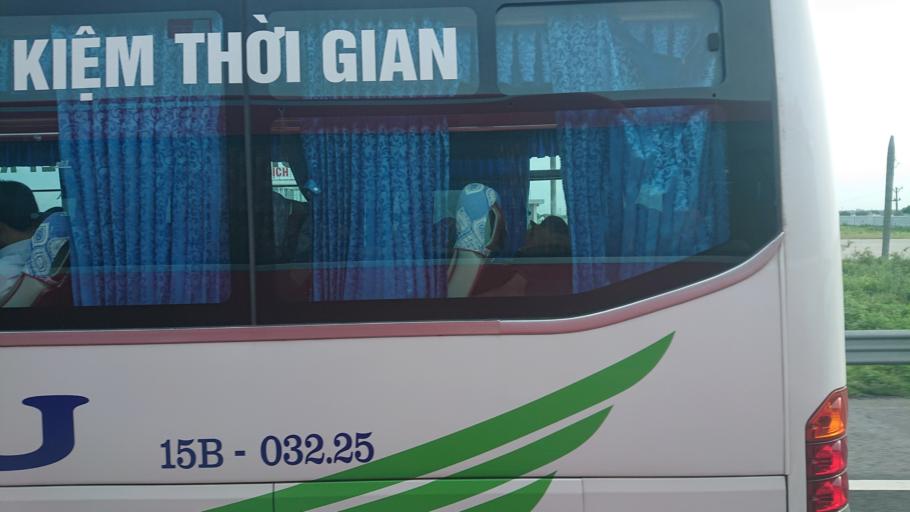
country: VN
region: Hai Phong
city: An Lao
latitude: 20.7938
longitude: 106.5475
